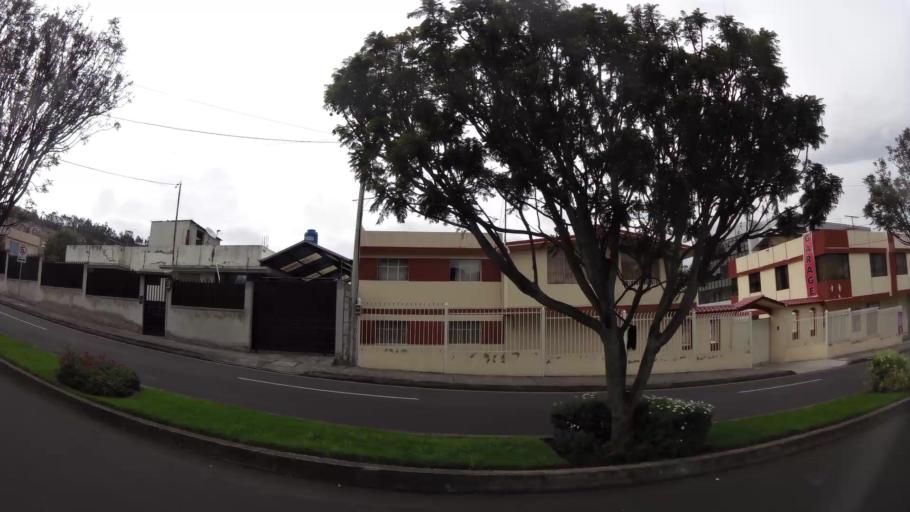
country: EC
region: Tungurahua
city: Ambato
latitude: -1.2755
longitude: -78.6389
